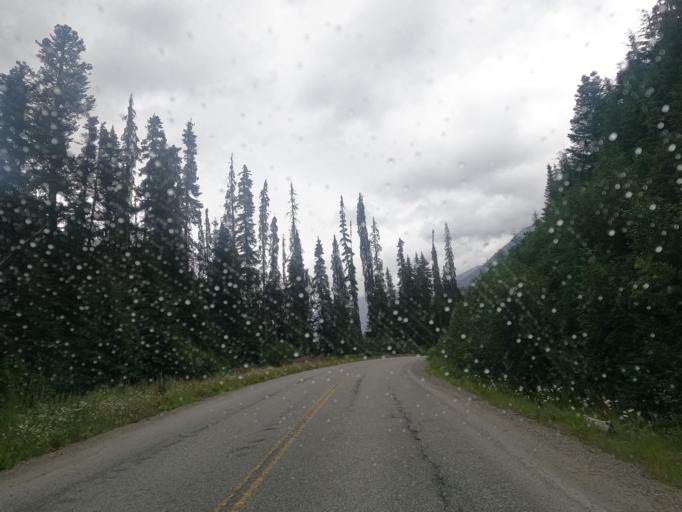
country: CA
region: British Columbia
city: Lillooet
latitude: 50.3978
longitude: -122.3191
